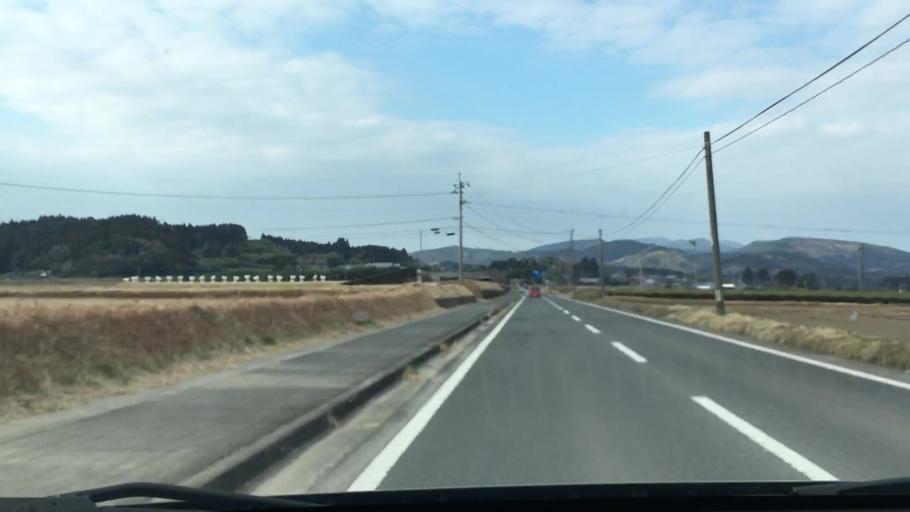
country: JP
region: Miyazaki
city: Kushima
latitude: 31.5165
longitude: 131.2392
